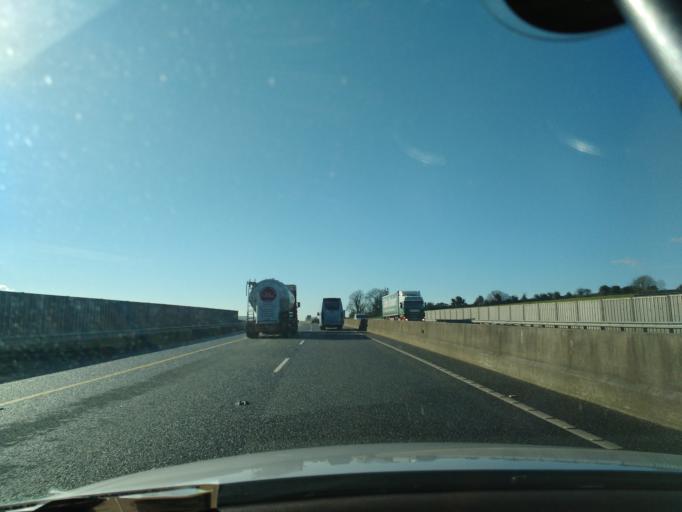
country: IE
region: Munster
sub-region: North Tipperary
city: Nenagh
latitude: 52.8374
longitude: -8.2844
